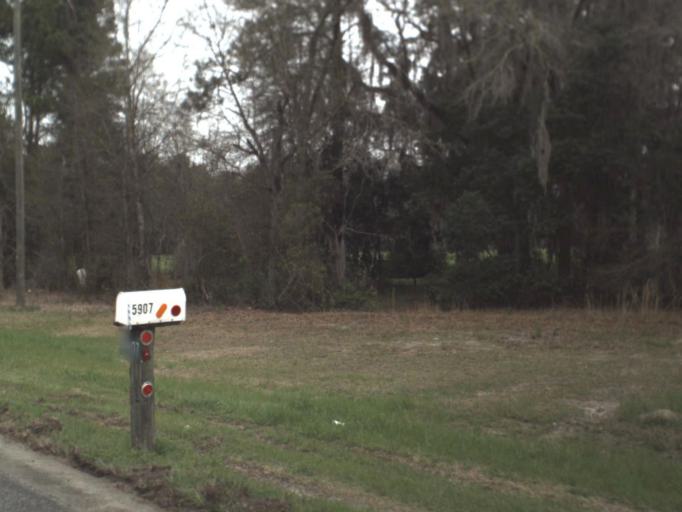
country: US
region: Florida
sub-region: Jefferson County
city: Monticello
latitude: 30.5167
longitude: -83.7819
